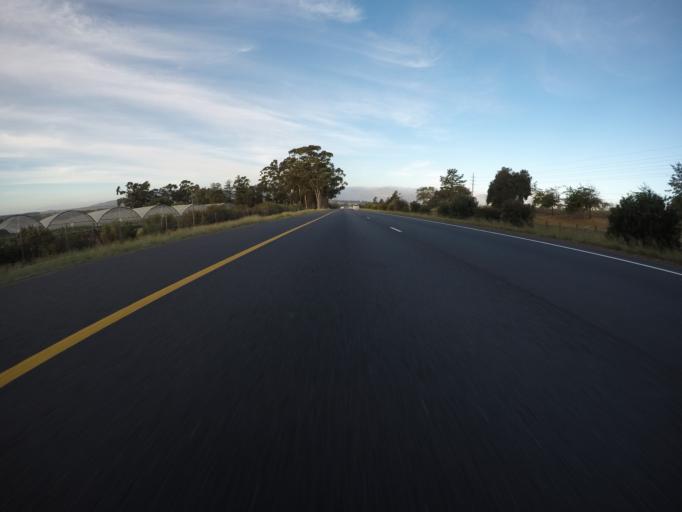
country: ZA
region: Western Cape
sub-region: City of Cape Town
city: Kraaifontein
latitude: -33.8058
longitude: 18.8413
